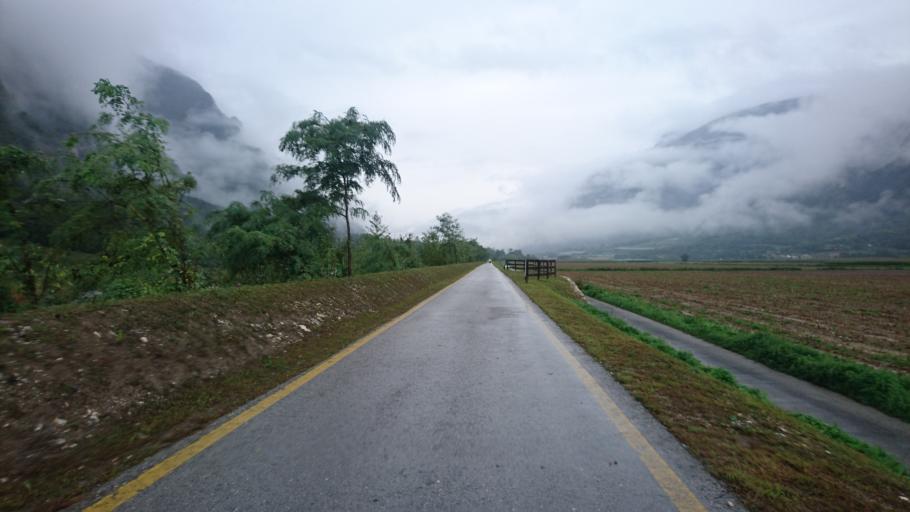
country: IT
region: Trentino-Alto Adige
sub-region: Provincia di Trento
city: Ospedaletto
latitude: 46.0229
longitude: 11.5788
